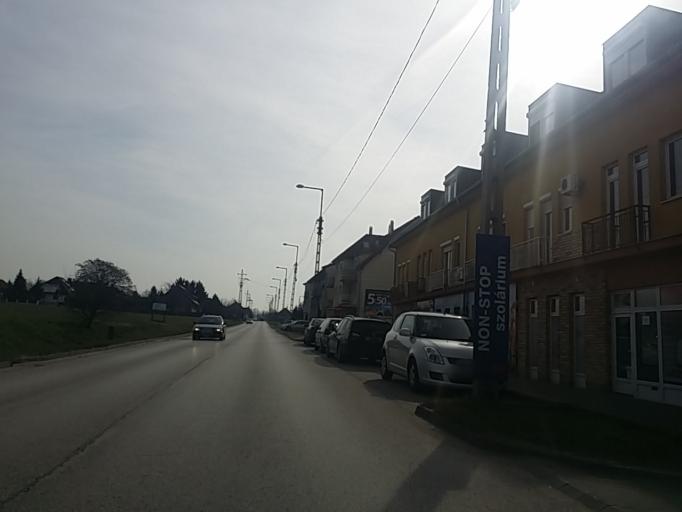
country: HU
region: Pest
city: Fot
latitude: 47.6188
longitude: 19.1925
